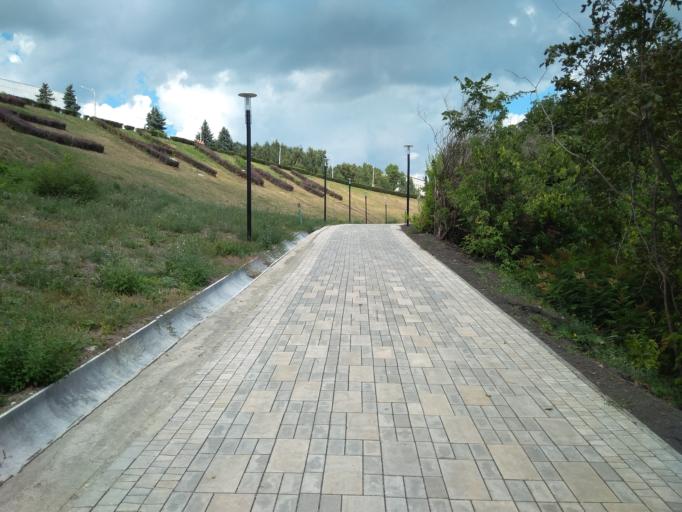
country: RU
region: Ulyanovsk
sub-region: Ulyanovskiy Rayon
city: Ulyanovsk
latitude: 54.3186
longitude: 48.4088
